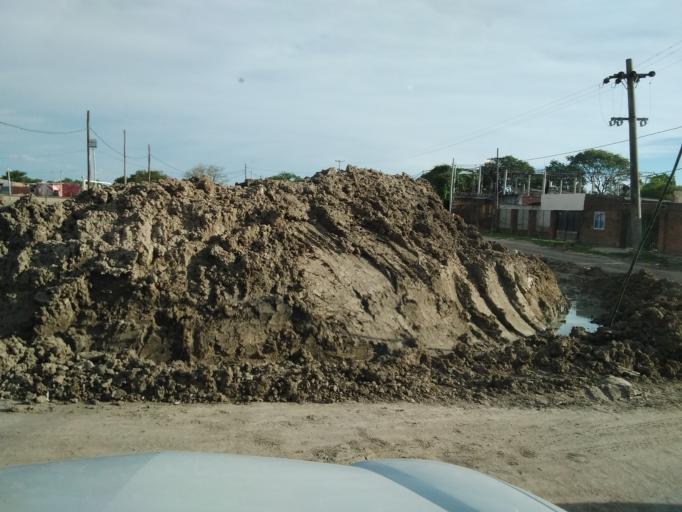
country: AR
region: Corrientes
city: Corrientes
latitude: -27.4926
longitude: -58.8456
